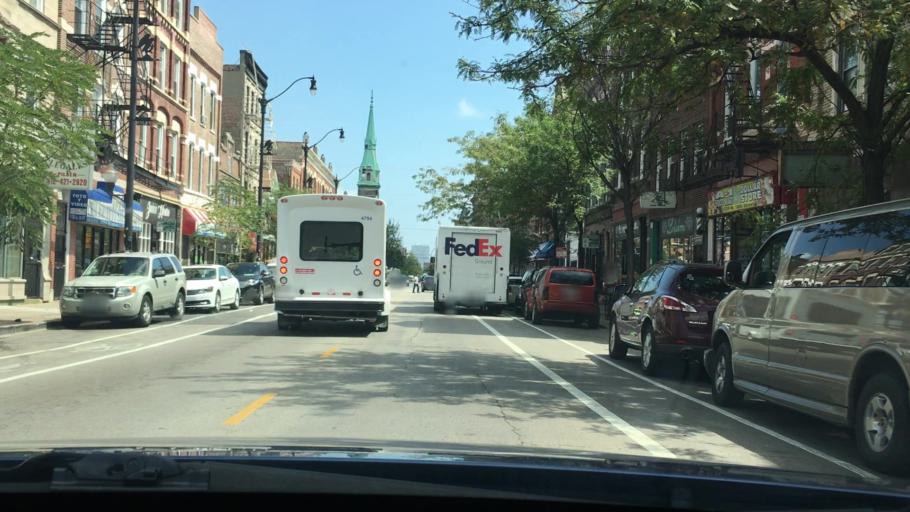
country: US
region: Illinois
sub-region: Cook County
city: Chicago
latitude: 41.8579
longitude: -87.6604
